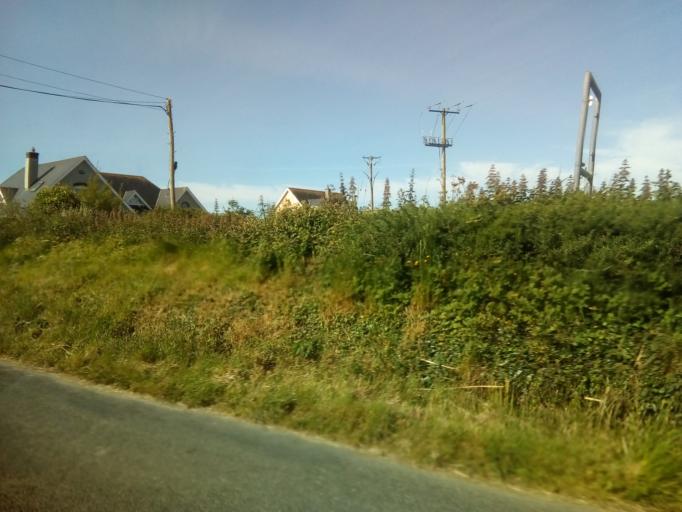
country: IE
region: Leinster
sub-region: Loch Garman
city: Loch Garman
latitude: 52.2148
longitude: -6.5415
